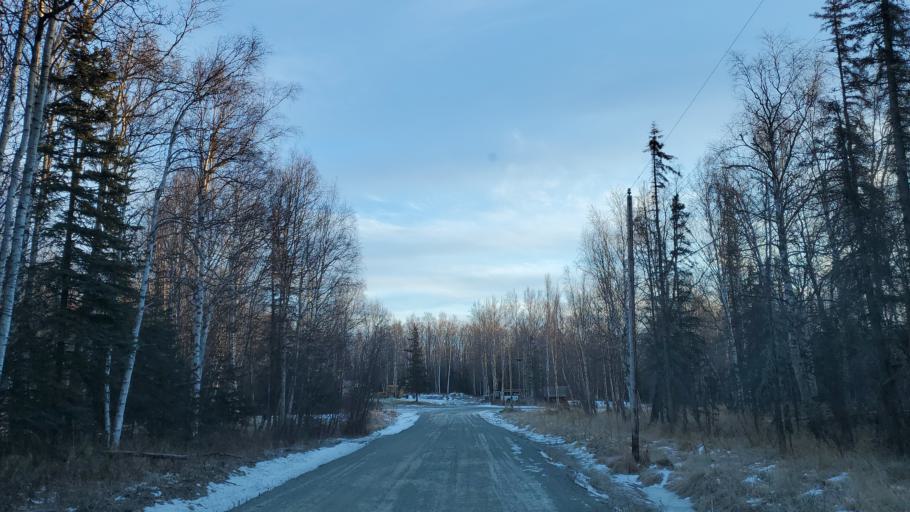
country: US
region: Alaska
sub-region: Matanuska-Susitna Borough
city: Lakes
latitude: 61.6530
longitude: -149.3182
